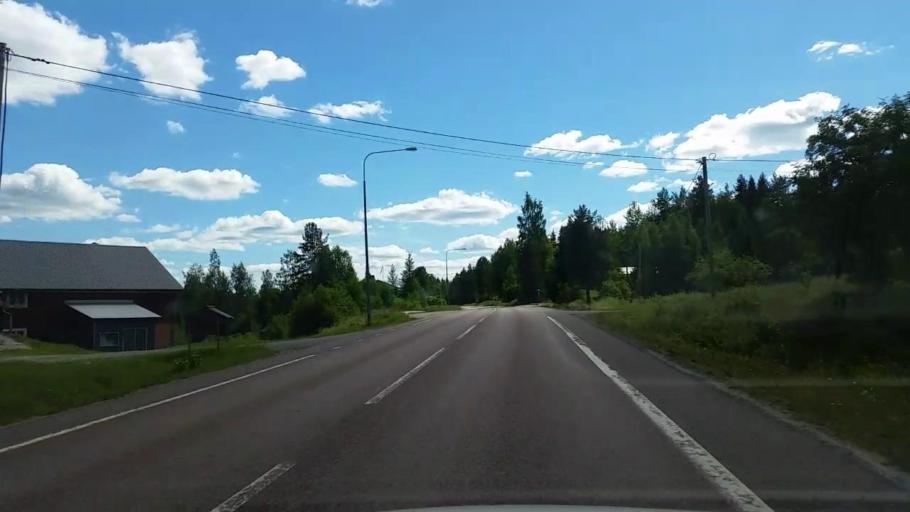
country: SE
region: Dalarna
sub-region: Faluns Kommun
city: Svardsjo
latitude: 60.8391
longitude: 15.7610
